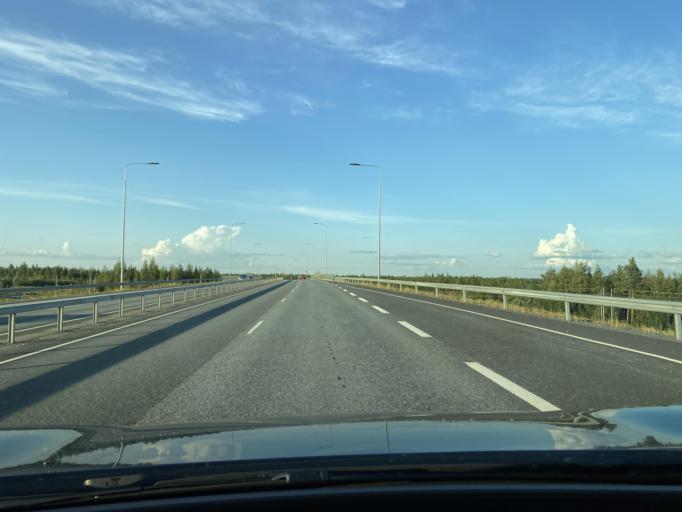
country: FI
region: Southern Ostrobothnia
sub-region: Seinaejoki
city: Nurmo
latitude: 62.7394
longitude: 22.9167
